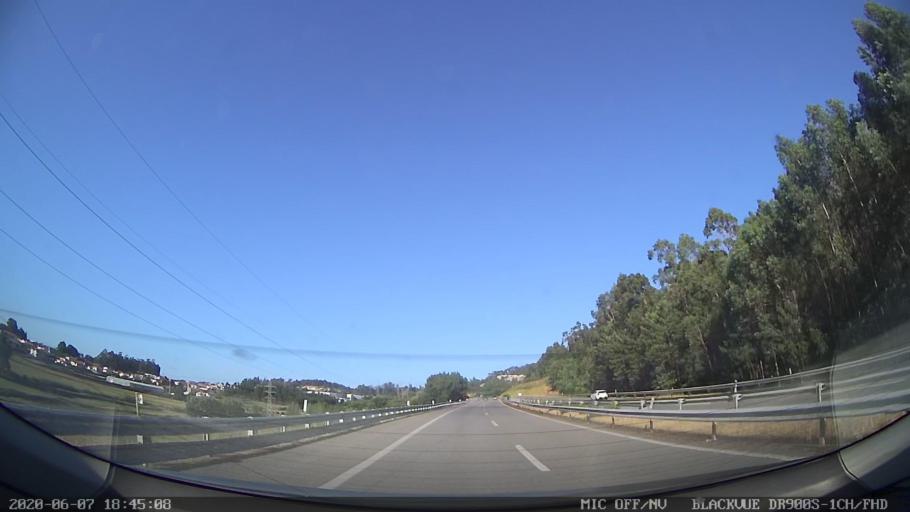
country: PT
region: Braga
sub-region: Vila Nova de Famalicao
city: Joane
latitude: 41.4064
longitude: -8.4327
